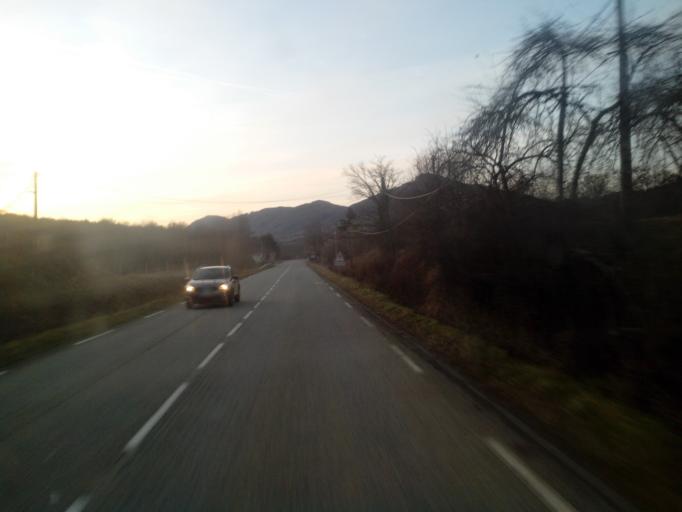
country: FR
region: Midi-Pyrenees
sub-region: Departement de l'Ariege
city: Saint-Paul-de-Jarrat
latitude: 42.9269
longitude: 1.7428
